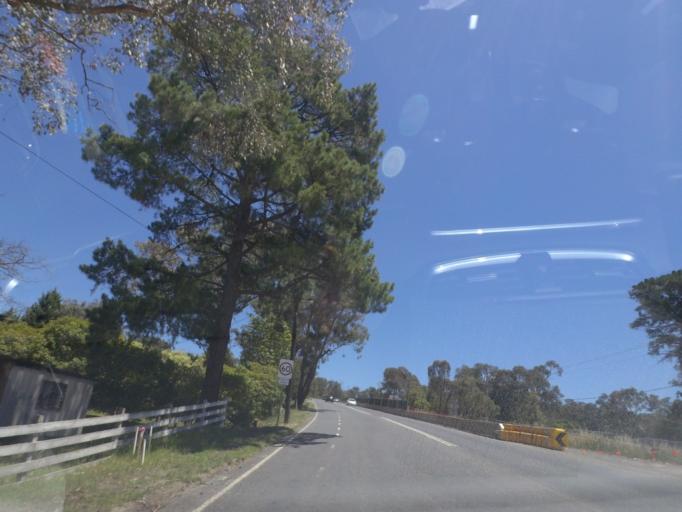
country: AU
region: Victoria
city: Plenty
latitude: -37.6552
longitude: 145.1238
